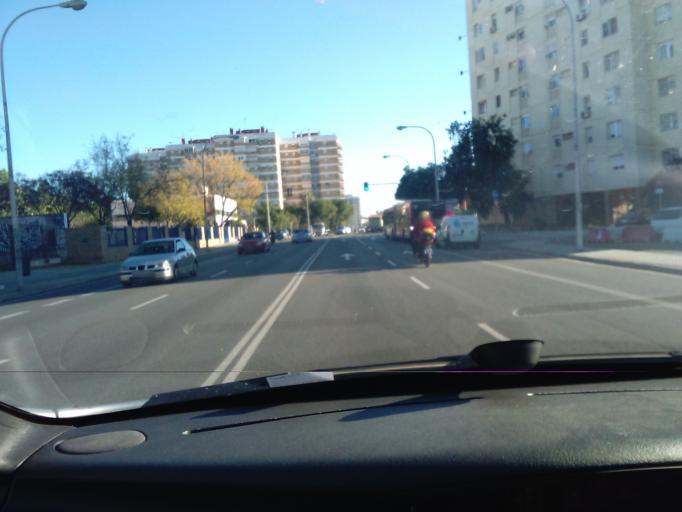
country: ES
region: Andalusia
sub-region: Provincia de Sevilla
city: Sevilla
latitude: 37.3947
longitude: -5.9635
